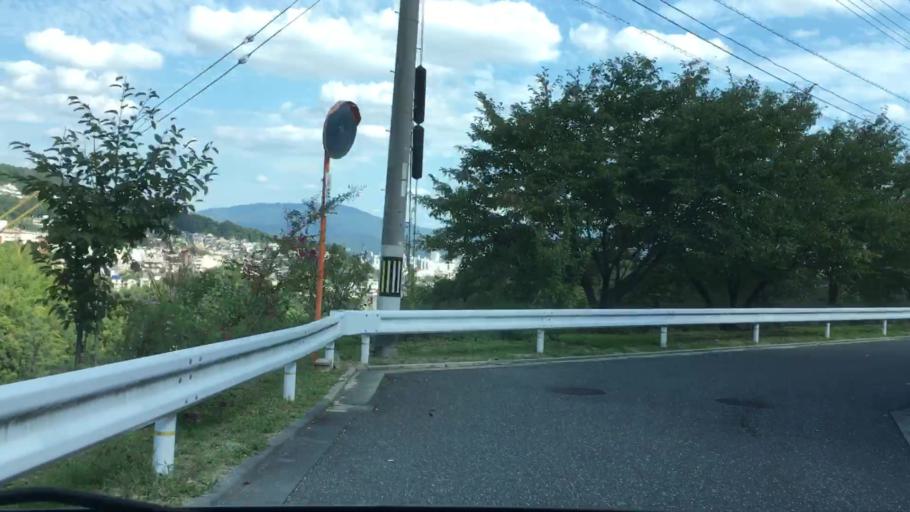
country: JP
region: Hiroshima
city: Hiroshima-shi
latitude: 34.4020
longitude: 132.4147
